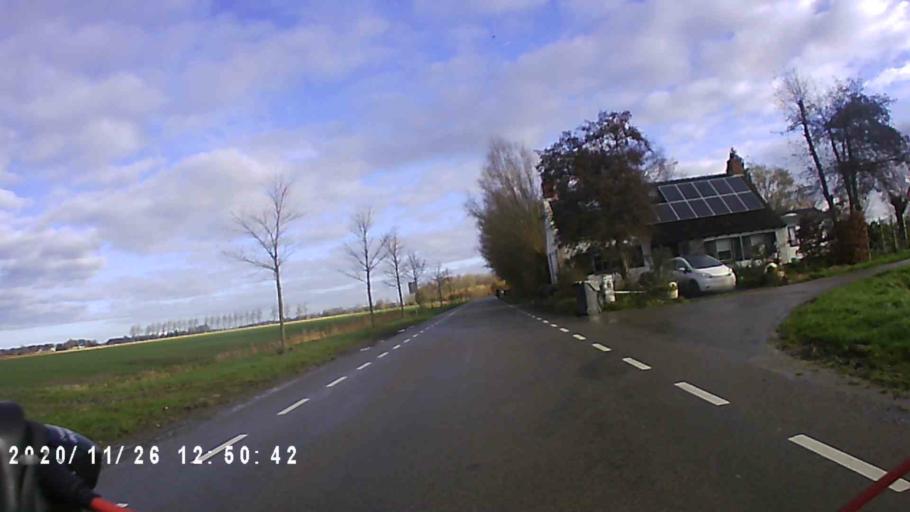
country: NL
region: Groningen
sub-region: Gemeente Appingedam
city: Appingedam
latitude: 53.3511
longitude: 6.7786
